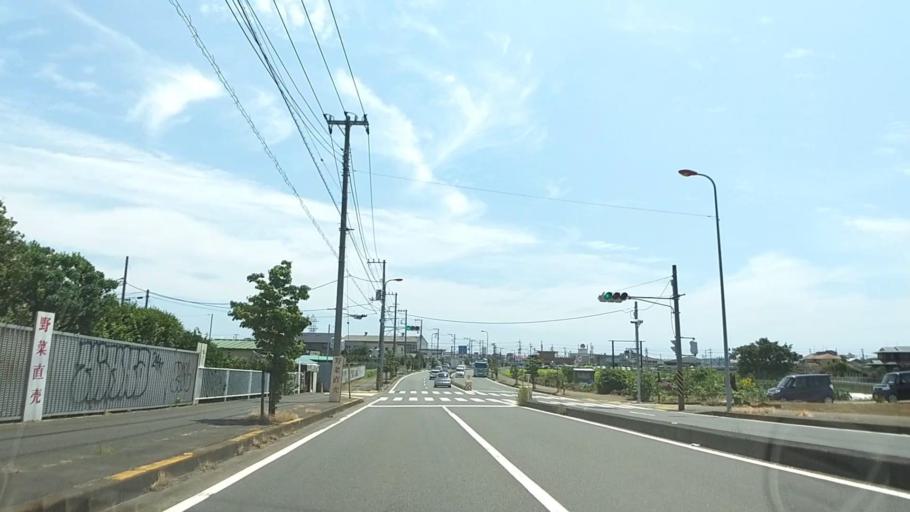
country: JP
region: Kanagawa
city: Atsugi
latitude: 35.4097
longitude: 139.3827
